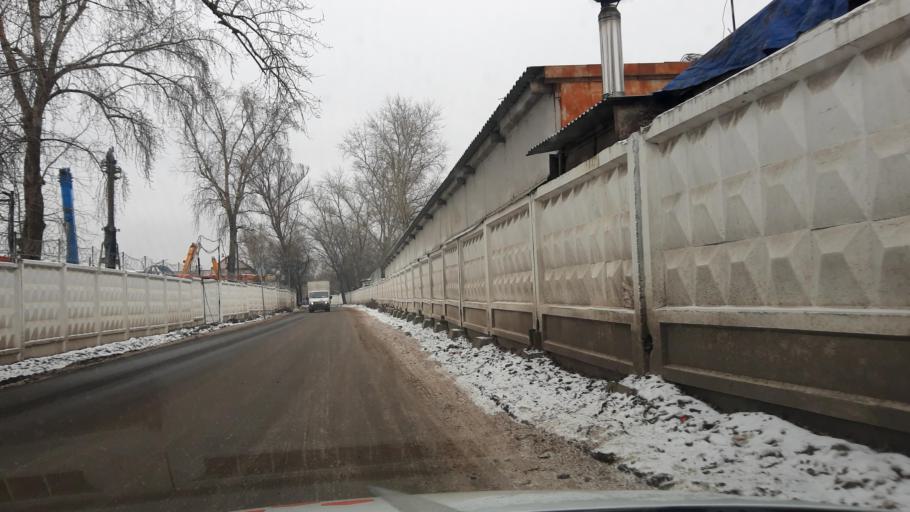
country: RU
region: Moscow
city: Lyublino
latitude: 55.6697
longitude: 37.7326
